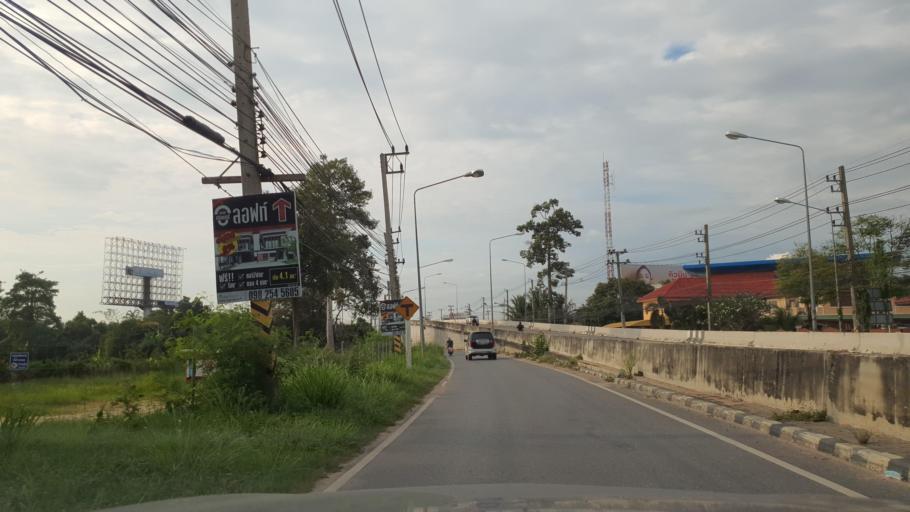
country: TH
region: Chon Buri
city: Phatthaya
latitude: 12.9474
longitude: 100.9364
